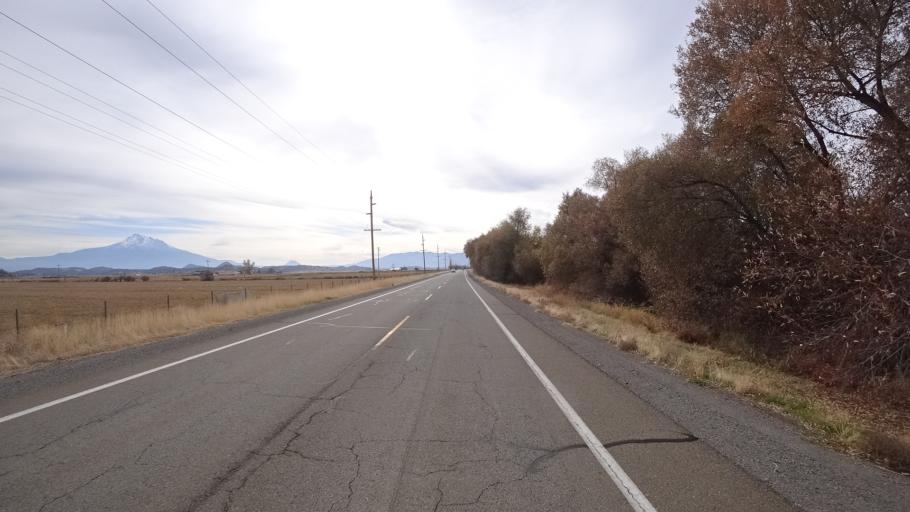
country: US
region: California
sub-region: Siskiyou County
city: Montague
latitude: 41.6522
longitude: -122.5203
